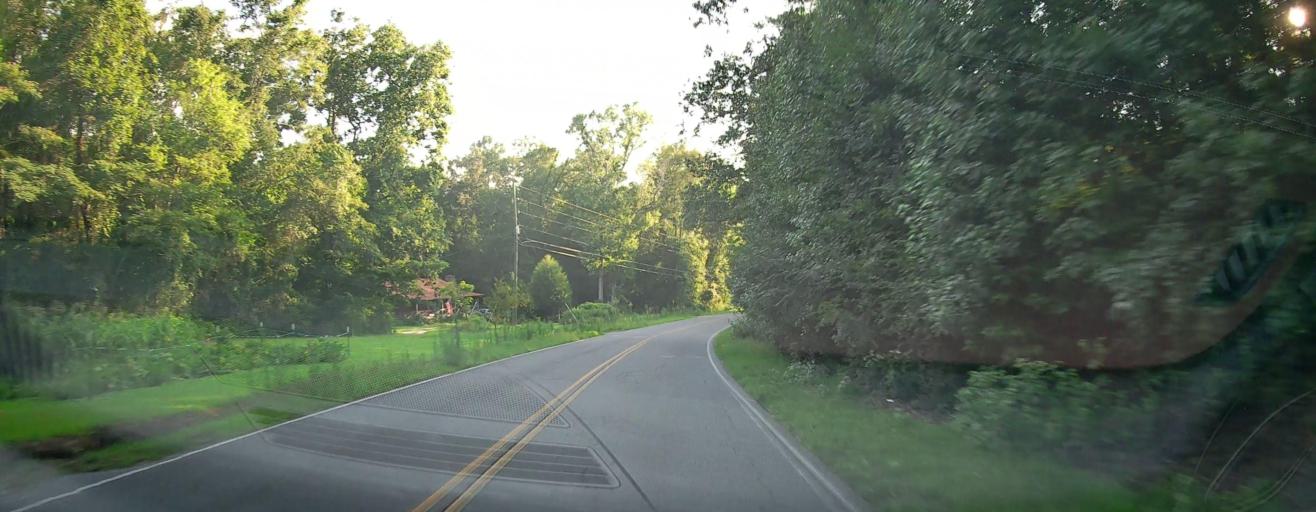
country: US
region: Georgia
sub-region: Peach County
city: Byron
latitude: 32.7265
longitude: -83.7521
